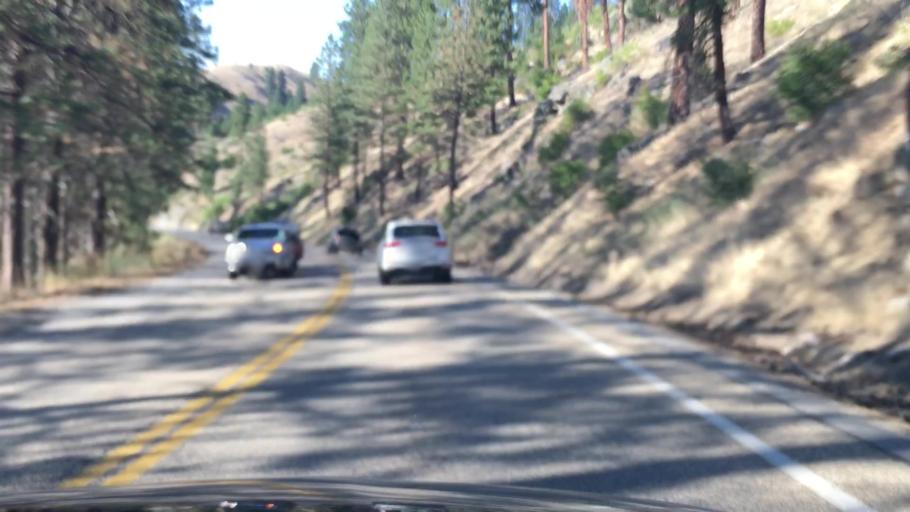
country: US
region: Idaho
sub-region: Boise County
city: Idaho City
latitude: 44.0695
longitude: -116.1189
